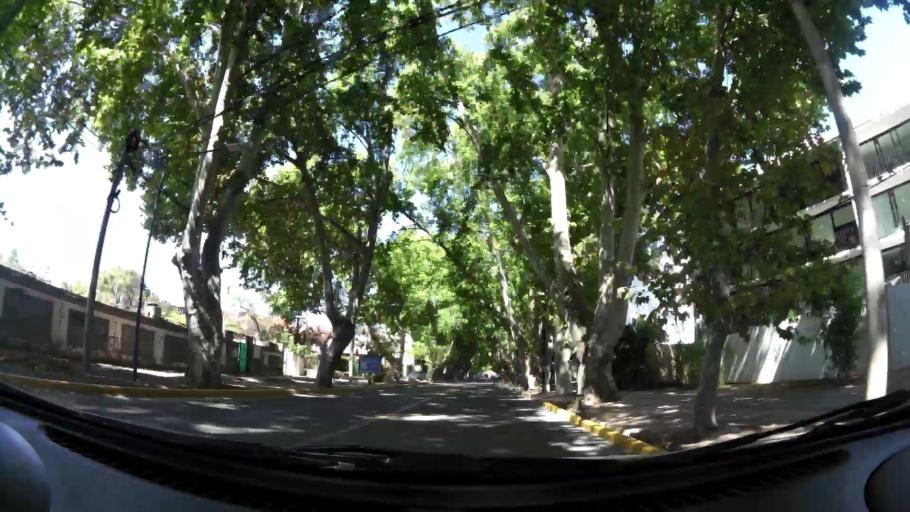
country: AR
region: Mendoza
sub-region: Departamento de Godoy Cruz
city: Godoy Cruz
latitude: -32.9498
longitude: -68.8496
